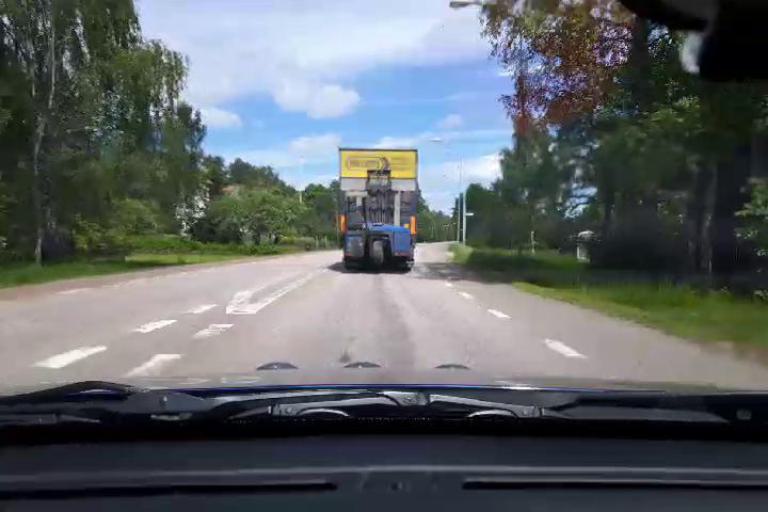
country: SE
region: Uppsala
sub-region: Osthammars Kommun
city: Bjorklinge
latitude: 60.0874
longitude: 17.5519
